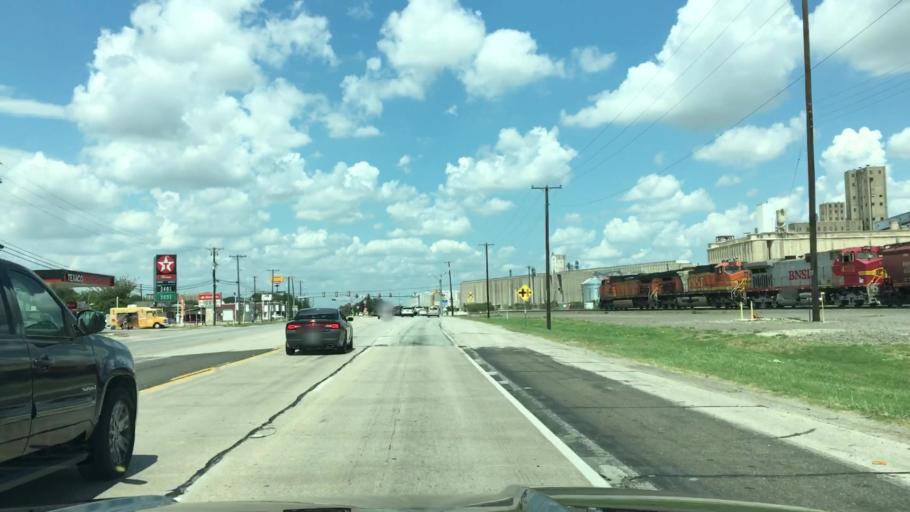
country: US
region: Texas
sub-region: Tarrant County
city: Saginaw
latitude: 32.8456
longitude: -97.3600
